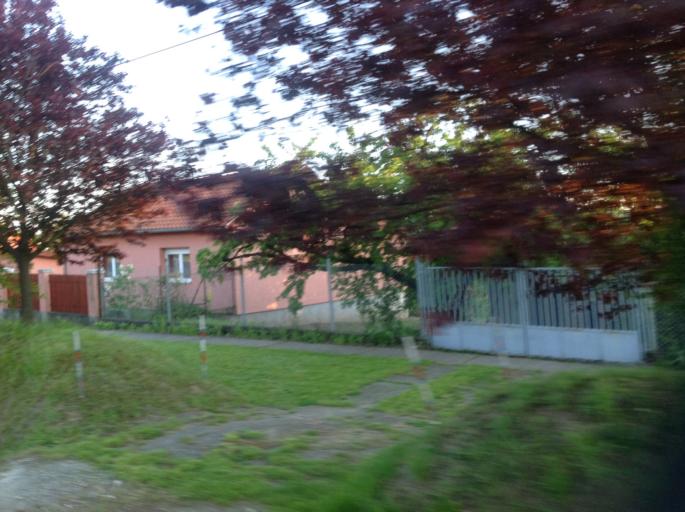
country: HU
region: Komarom-Esztergom
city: Sarisap
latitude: 47.6658
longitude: 18.6933
